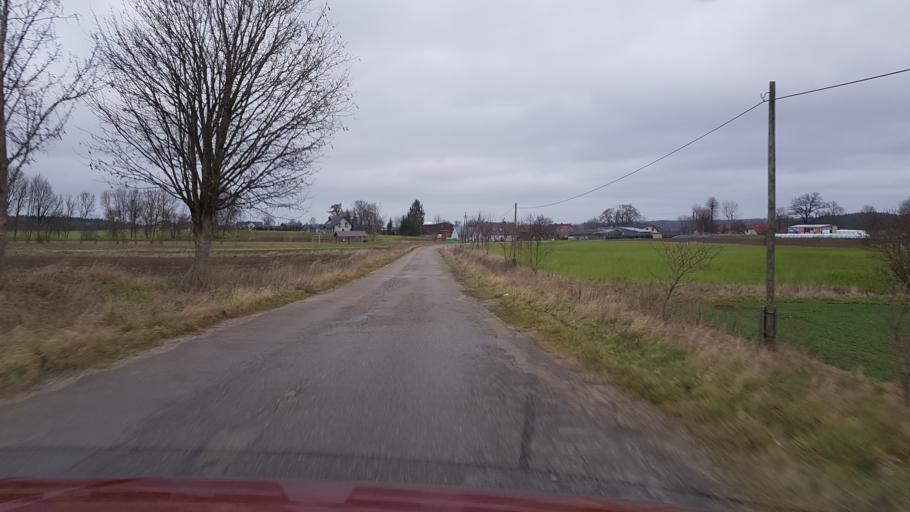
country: PL
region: Pomeranian Voivodeship
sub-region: Powiat bytowski
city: Borzytuchom
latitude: 54.1770
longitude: 17.3564
